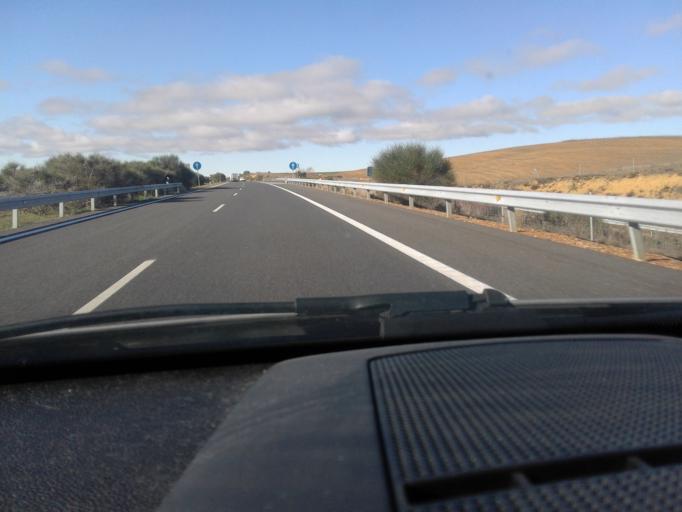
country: ES
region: Castille and Leon
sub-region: Provincia de Palencia
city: Ledigos
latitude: 42.3674
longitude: -4.8751
